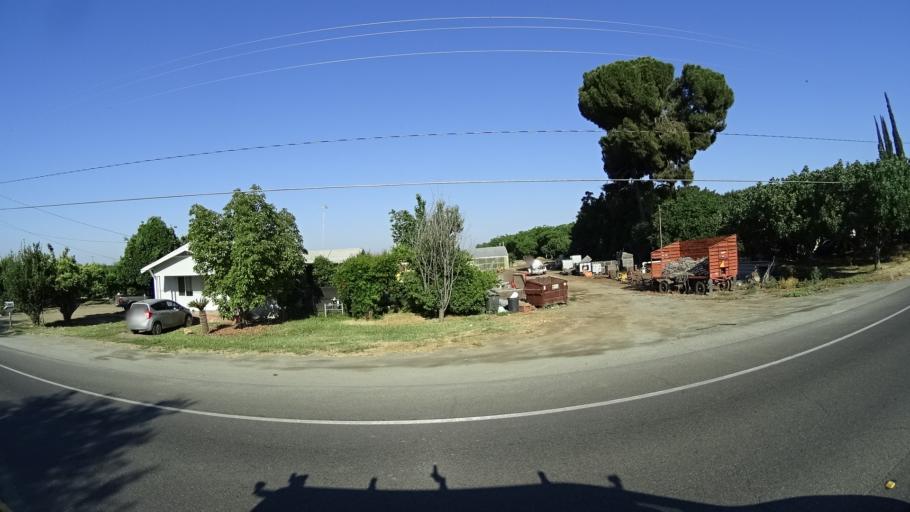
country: US
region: California
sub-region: Kings County
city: Armona
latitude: 36.3405
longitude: -119.7090
